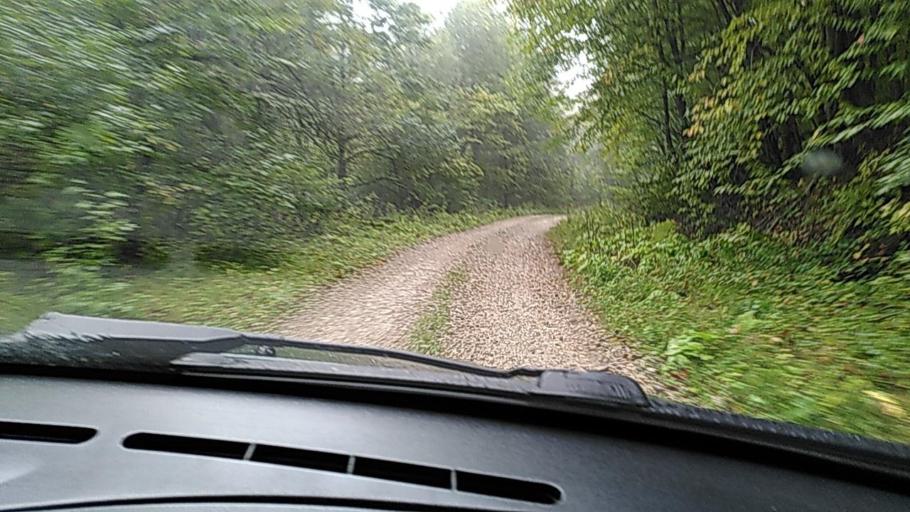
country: RU
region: Kabardino-Balkariya
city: Belaya Rechka
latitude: 43.3727
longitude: 43.4271
